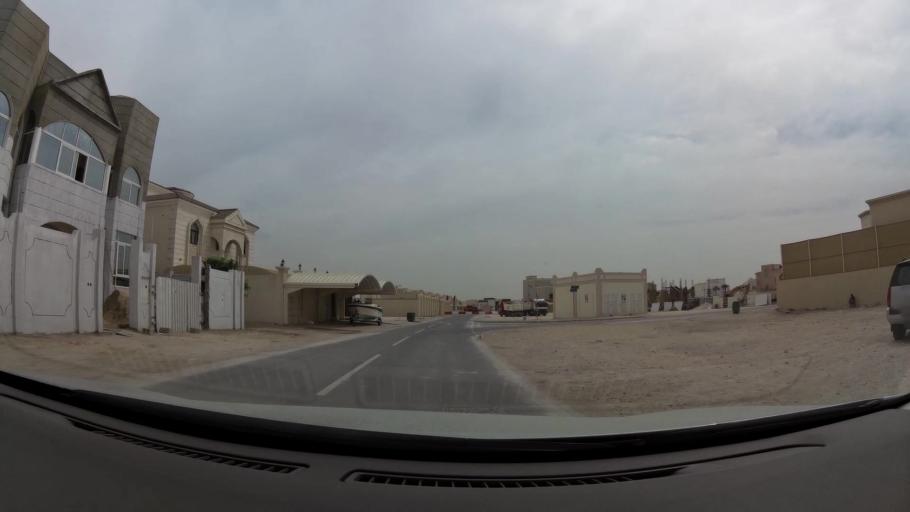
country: QA
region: Baladiyat ar Rayyan
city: Ar Rayyan
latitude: 25.2199
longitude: 51.4644
